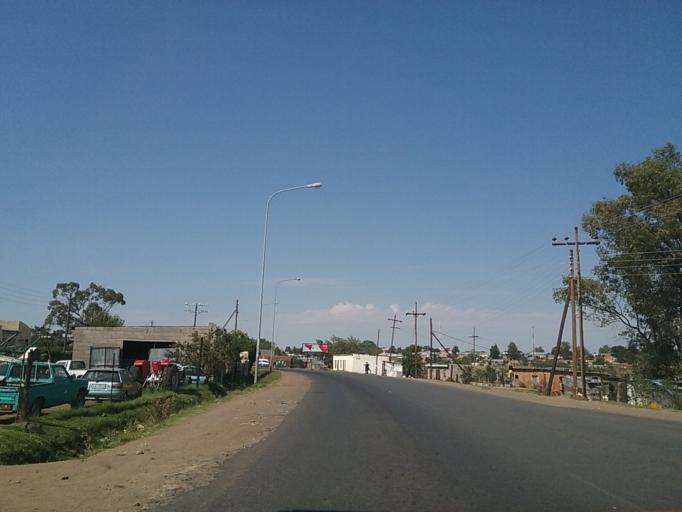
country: LS
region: Berea
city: Teyateyaneng
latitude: -29.1445
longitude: 27.7493
